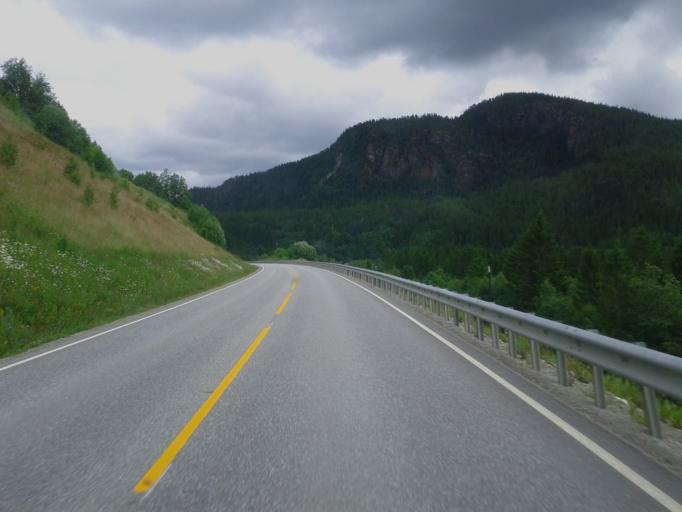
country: NO
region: Sor-Trondelag
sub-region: Midtre Gauldal
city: Storen
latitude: 62.9421
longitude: 10.6682
